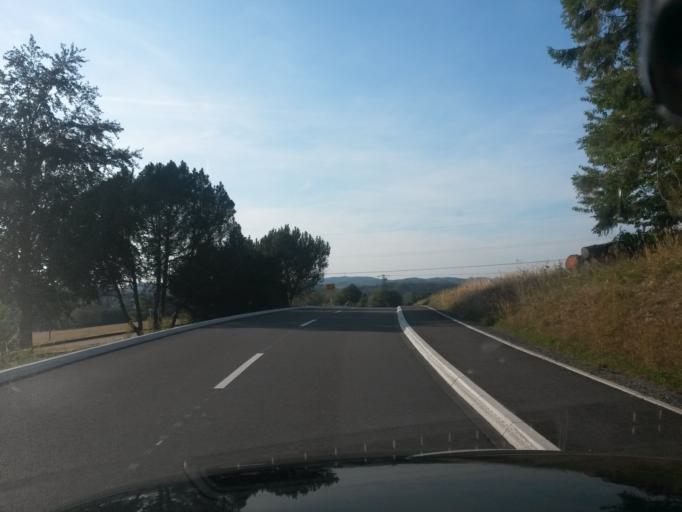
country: DE
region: North Rhine-Westphalia
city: Wiehl
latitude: 50.9826
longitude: 7.5738
